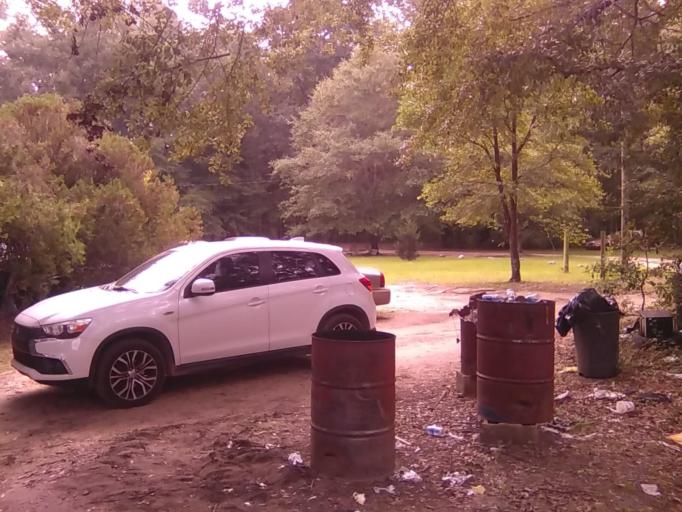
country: US
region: Alabama
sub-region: Dallas County
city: Selmont-West Selmont
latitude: 32.3731
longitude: -86.9990
